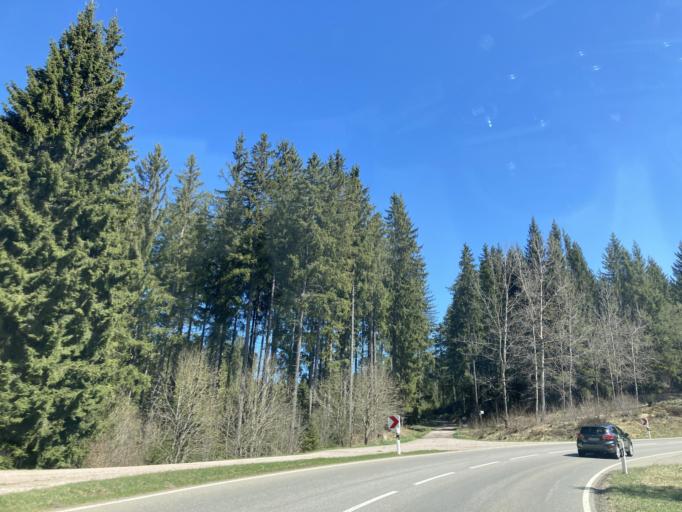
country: DE
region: Baden-Wuerttemberg
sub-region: Freiburg Region
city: Vohrenbach
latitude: 48.0388
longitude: 8.3378
